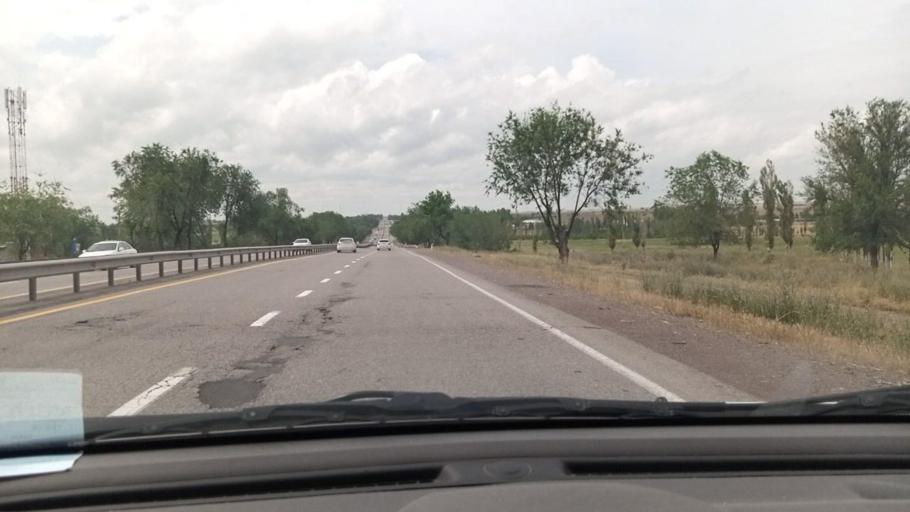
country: UZ
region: Toshkent
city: Tuytepa
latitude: 41.0186
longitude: 69.5138
